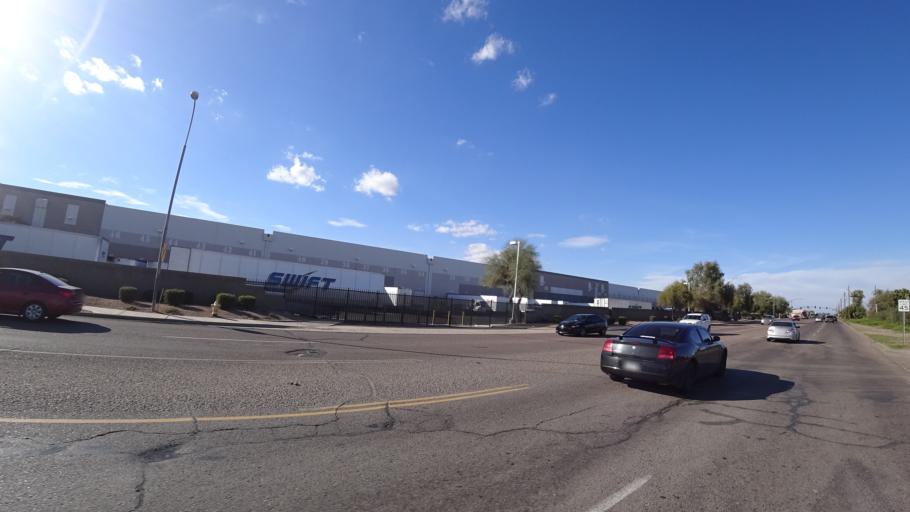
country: US
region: Arizona
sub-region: Maricopa County
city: Tolleson
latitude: 33.4446
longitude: -112.2383
